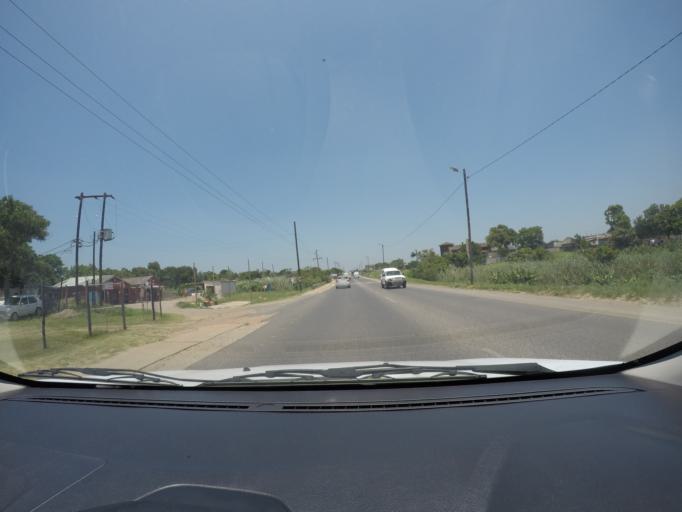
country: ZA
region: KwaZulu-Natal
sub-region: uThungulu District Municipality
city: eSikhawini
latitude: -28.8802
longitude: 31.9082
